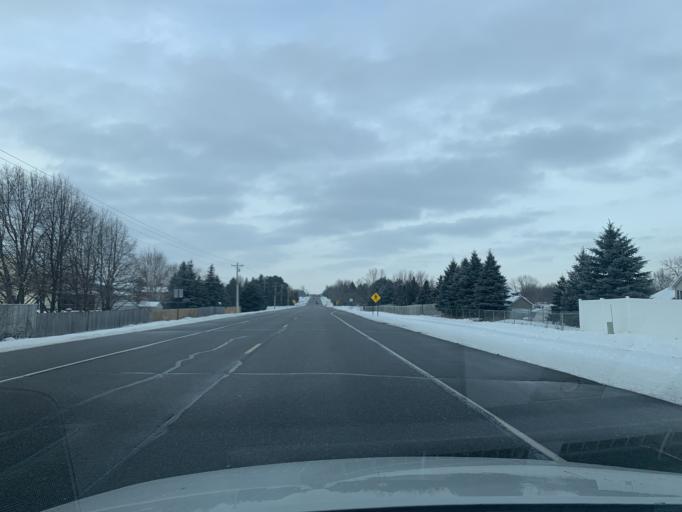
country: US
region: Minnesota
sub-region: Anoka County
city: Anoka
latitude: 45.2369
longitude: -93.4071
